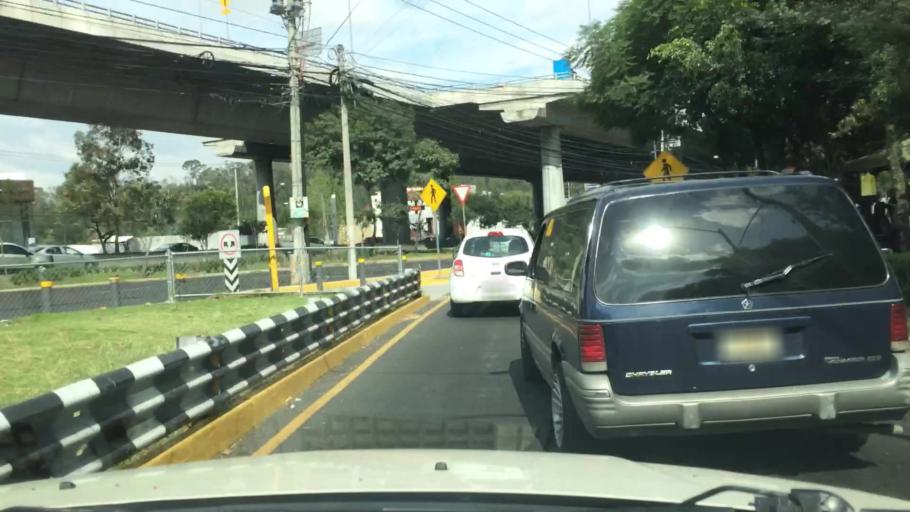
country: MX
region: Mexico City
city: Magdalena Contreras
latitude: 19.3050
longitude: -99.2044
